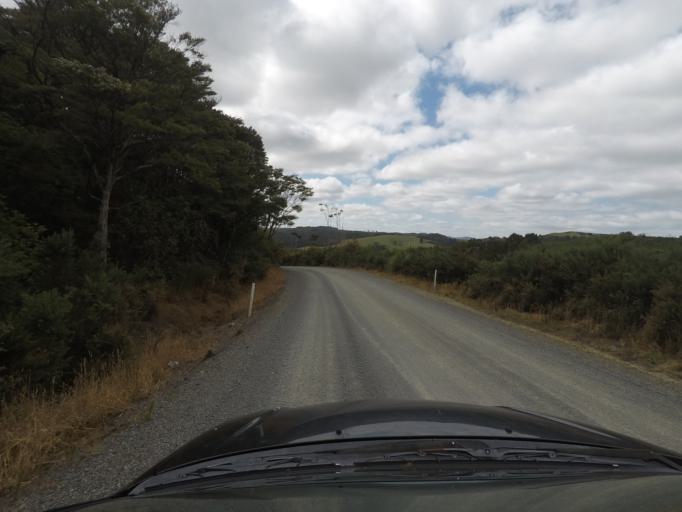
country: NZ
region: Northland
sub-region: Whangarei
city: Ruakaka
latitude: -35.9288
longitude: 174.3413
